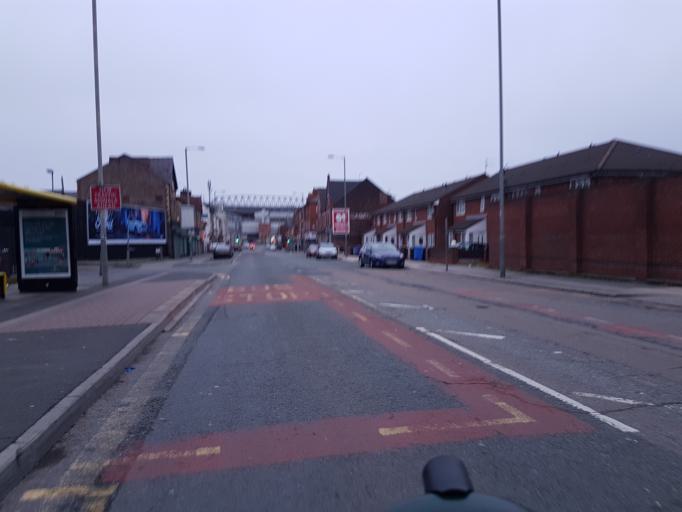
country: GB
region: England
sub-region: Liverpool
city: Liverpool
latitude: 53.4265
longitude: -2.9571
